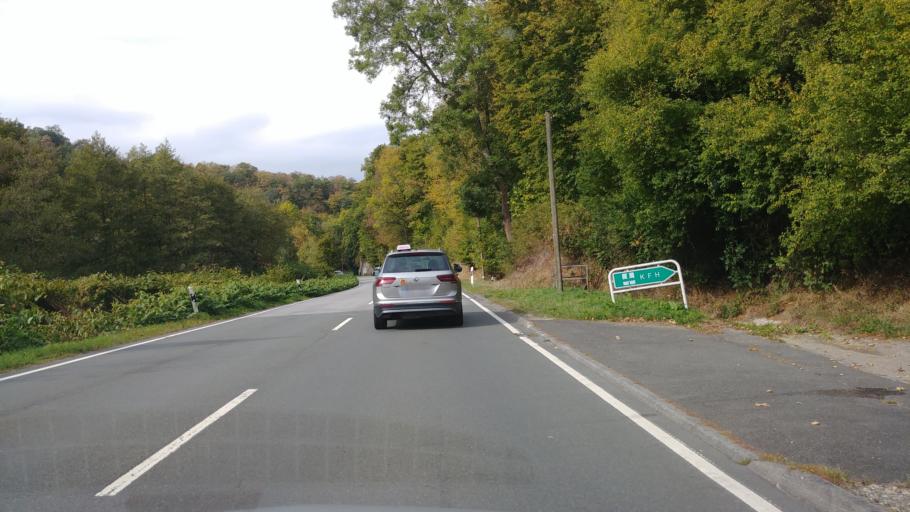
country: DE
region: Hesse
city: Burg Hohenstein
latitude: 50.1974
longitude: 8.0521
